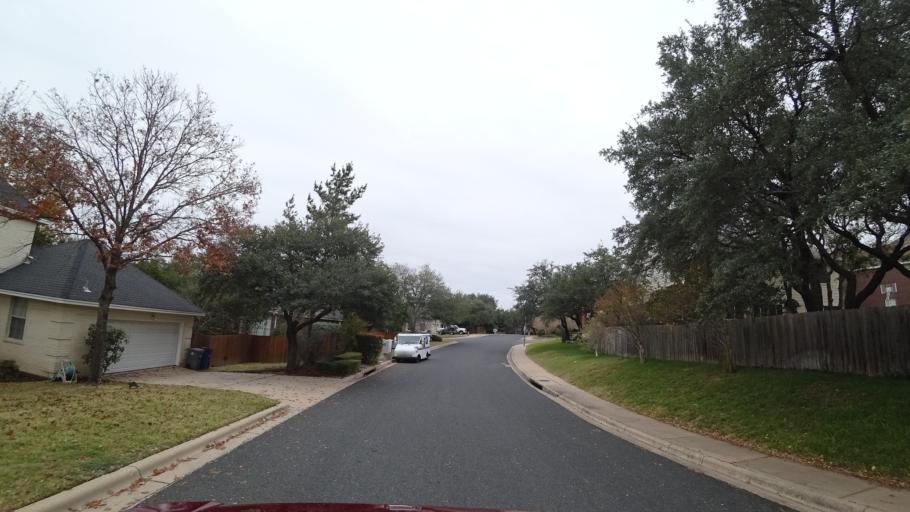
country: US
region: Texas
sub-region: Williamson County
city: Jollyville
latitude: 30.3822
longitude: -97.7972
